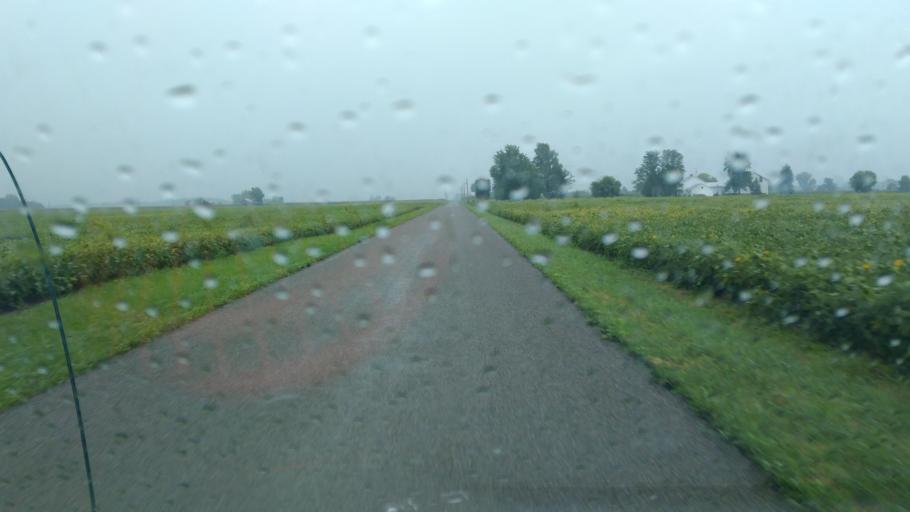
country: US
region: Ohio
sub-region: Hardin County
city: Kenton
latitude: 40.7155
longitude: -83.5950
